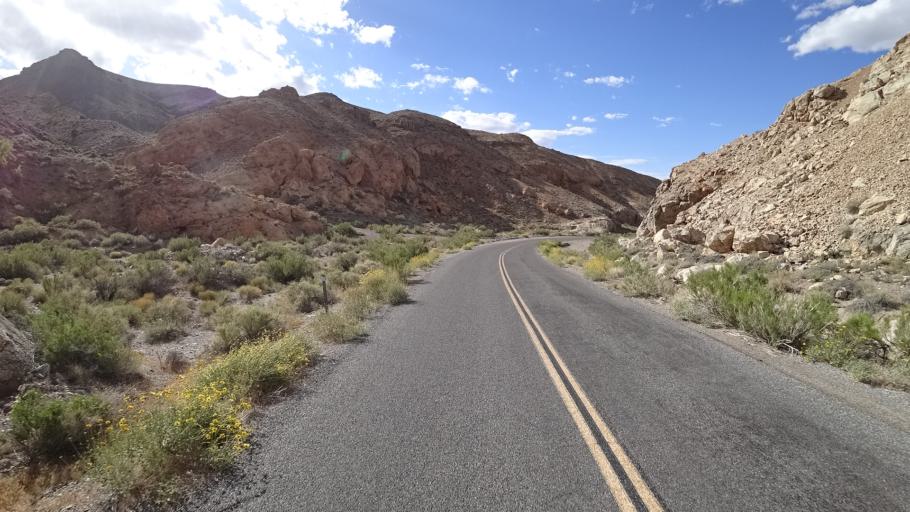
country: US
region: Nevada
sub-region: Nye County
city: Beatty
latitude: 36.4255
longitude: -117.1927
